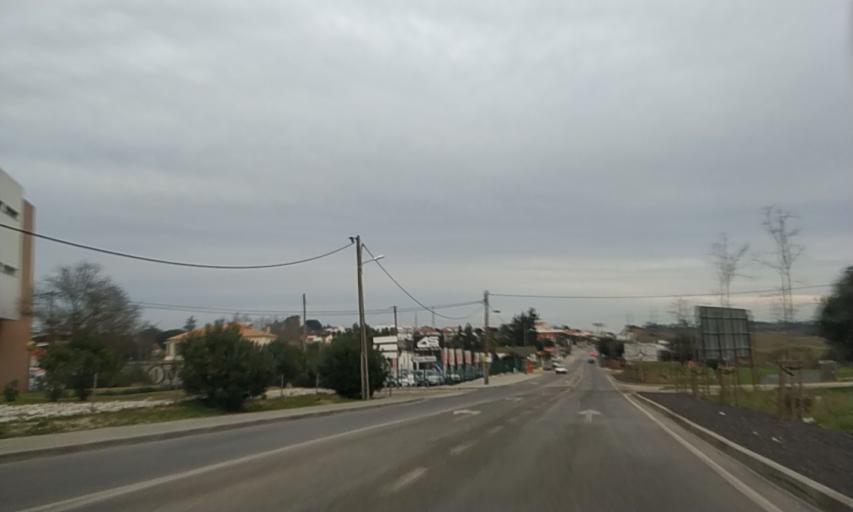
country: PT
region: Setubal
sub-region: Setubal
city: Setubal
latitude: 38.5375
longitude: -8.8561
